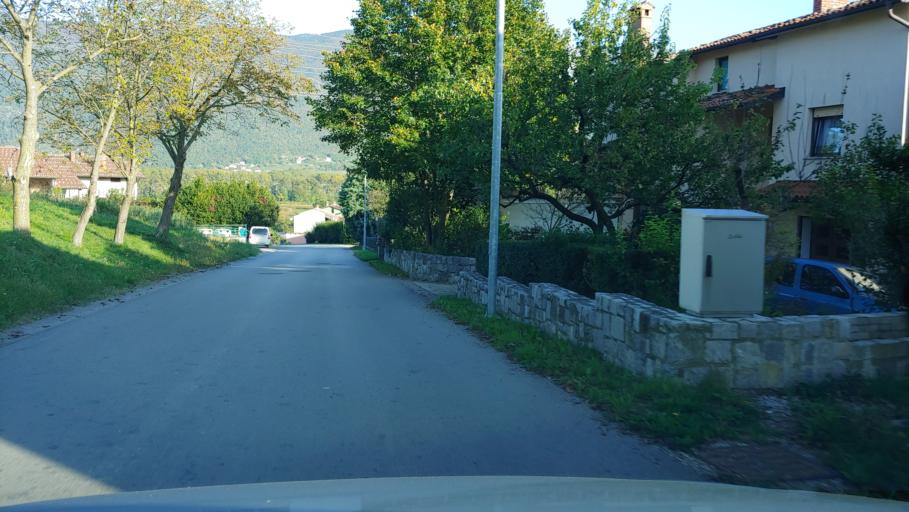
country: SI
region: Vipava
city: Vipava
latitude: 45.8402
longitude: 13.9366
